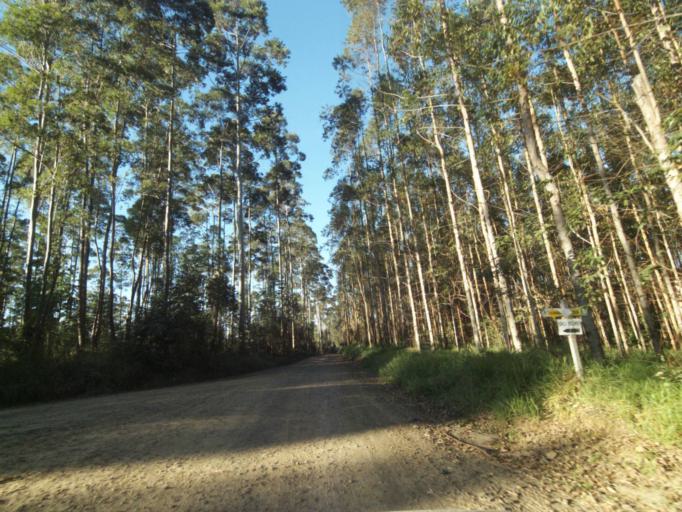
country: BR
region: Parana
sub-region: Telemaco Borba
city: Telemaco Borba
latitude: -24.4940
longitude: -50.5991
